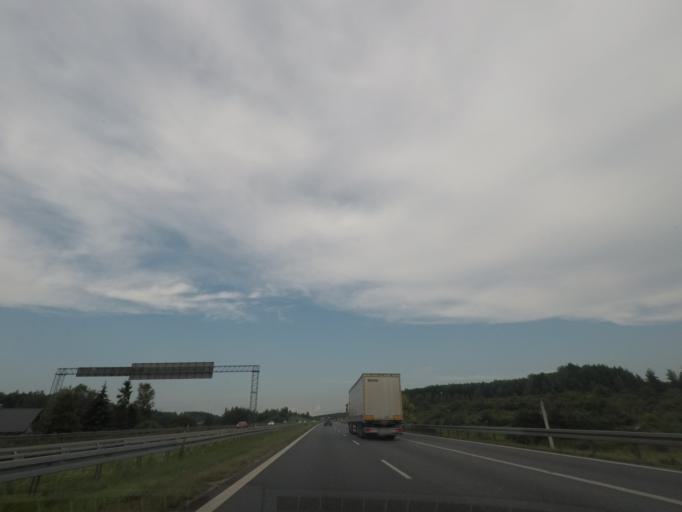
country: PL
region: Lesser Poland Voivodeship
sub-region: Powiat chrzanowski
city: Balin
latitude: 50.1522
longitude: 19.3497
